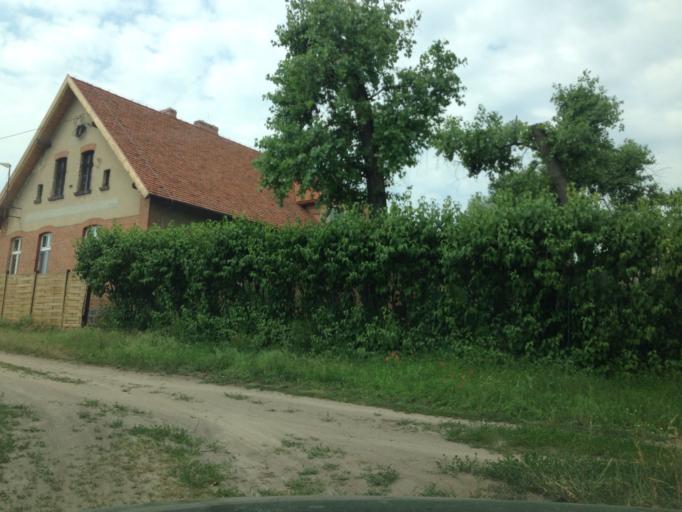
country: PL
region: Kujawsko-Pomorskie
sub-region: Powiat rypinski
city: Wapielsk
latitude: 53.2077
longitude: 19.2619
